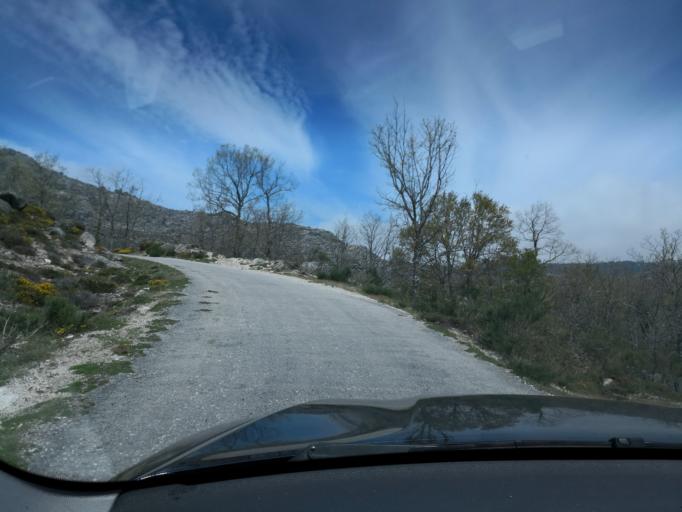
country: PT
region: Vila Real
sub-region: Vila Real
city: Vila Real
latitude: 41.3333
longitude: -7.8002
